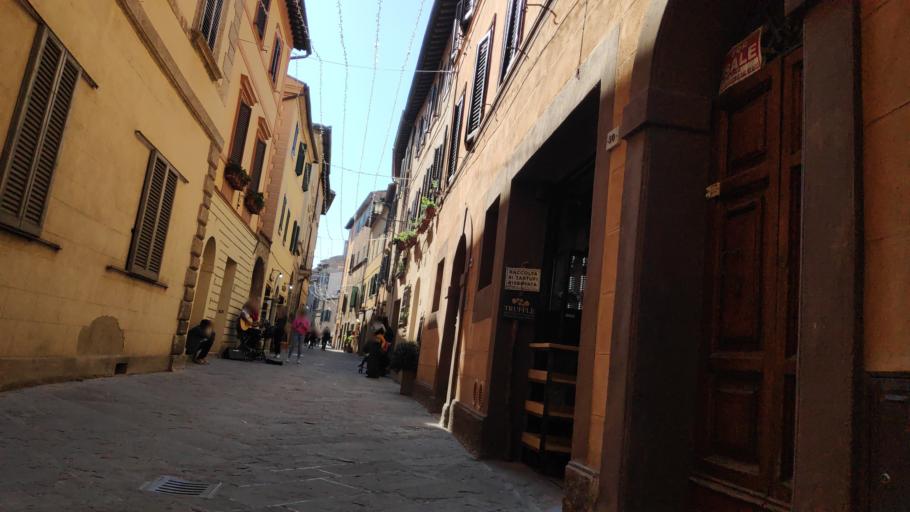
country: IT
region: Tuscany
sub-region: Provincia di Siena
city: Montepulciano
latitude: 43.0920
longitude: 11.7818
